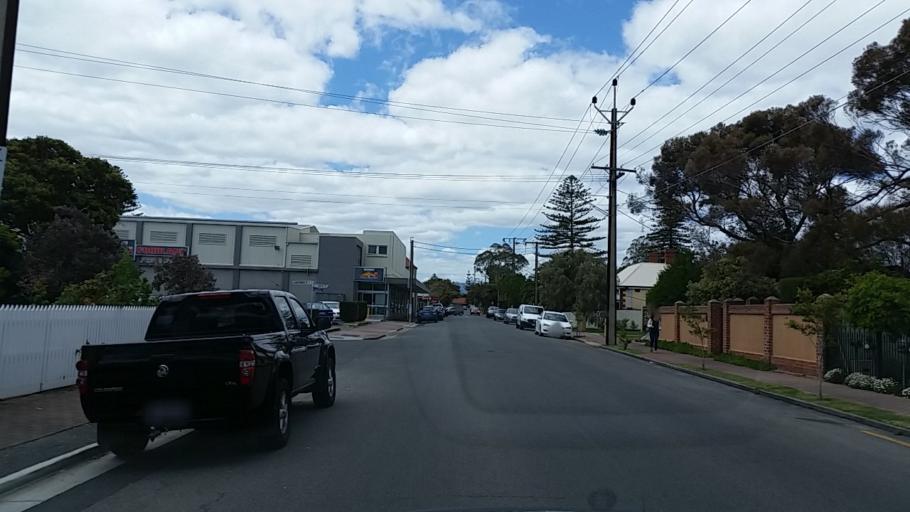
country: AU
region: South Australia
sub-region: Adelaide
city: Glenelg
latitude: -34.9904
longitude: 138.5170
